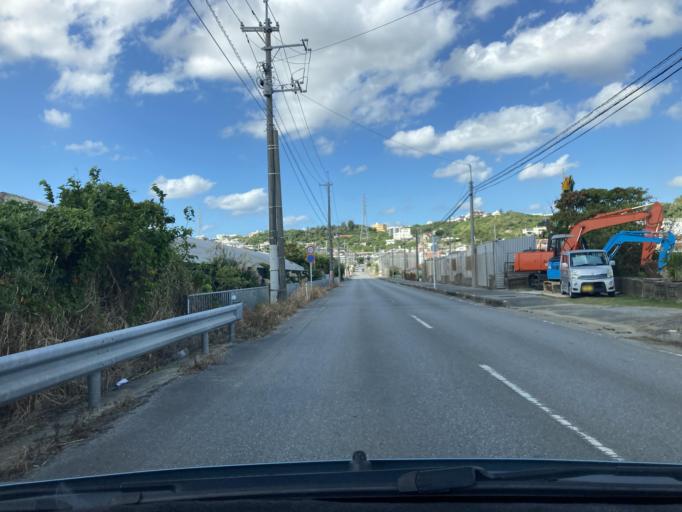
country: JP
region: Okinawa
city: Gushikawa
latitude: 26.3453
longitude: 127.8478
